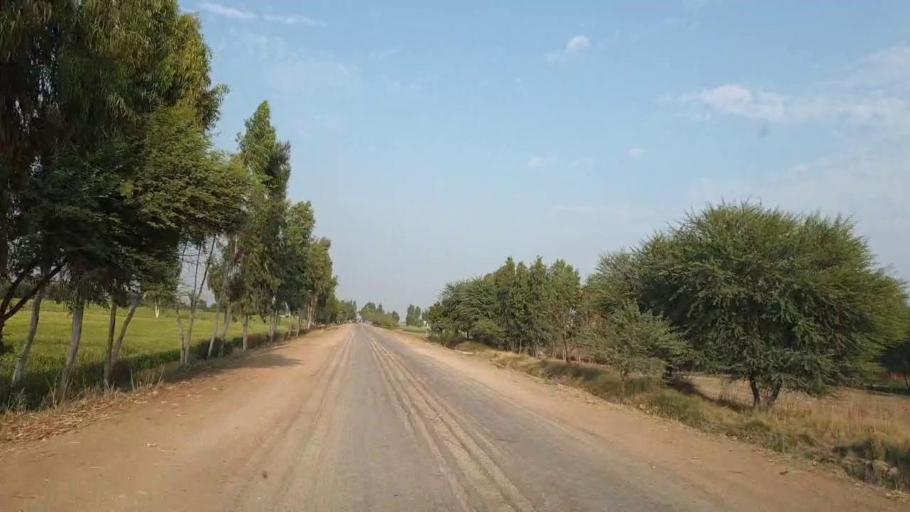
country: PK
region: Sindh
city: Pithoro
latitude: 25.5794
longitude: 69.2601
